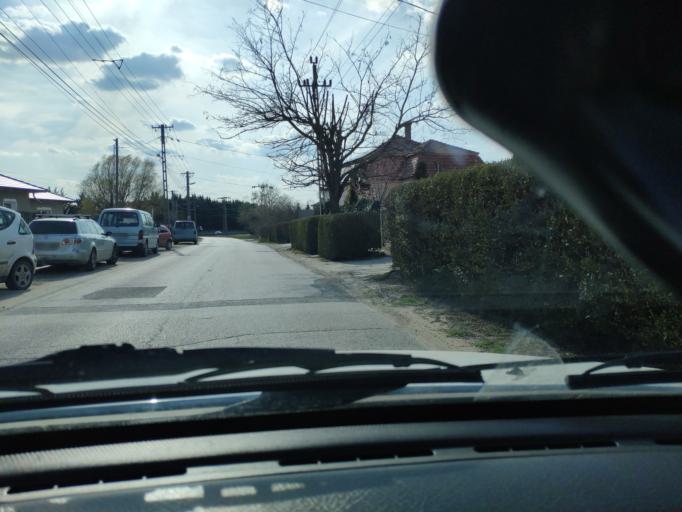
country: HU
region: Pest
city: Rackeve
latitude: 47.1583
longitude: 18.9356
